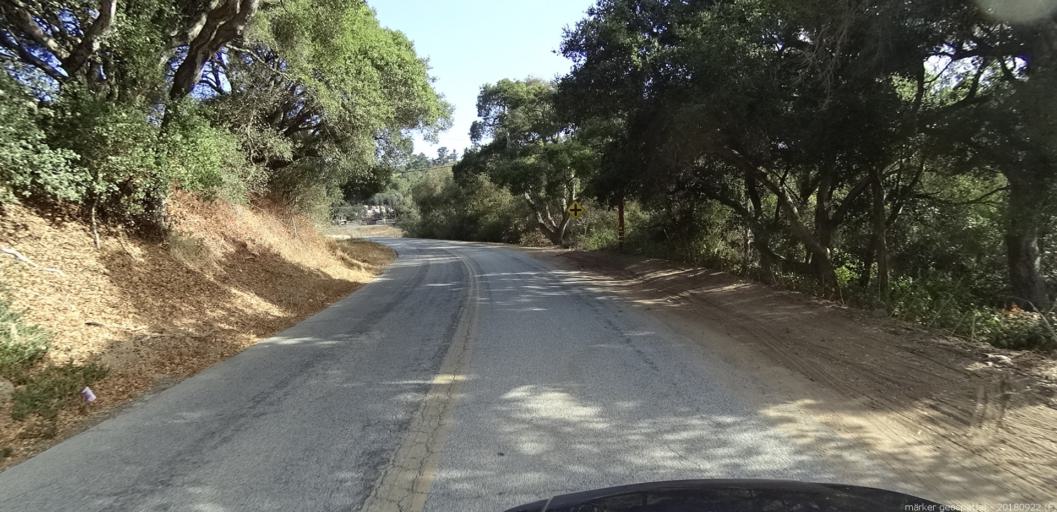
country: US
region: California
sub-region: Monterey County
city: Prunedale
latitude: 36.8071
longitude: -121.6493
